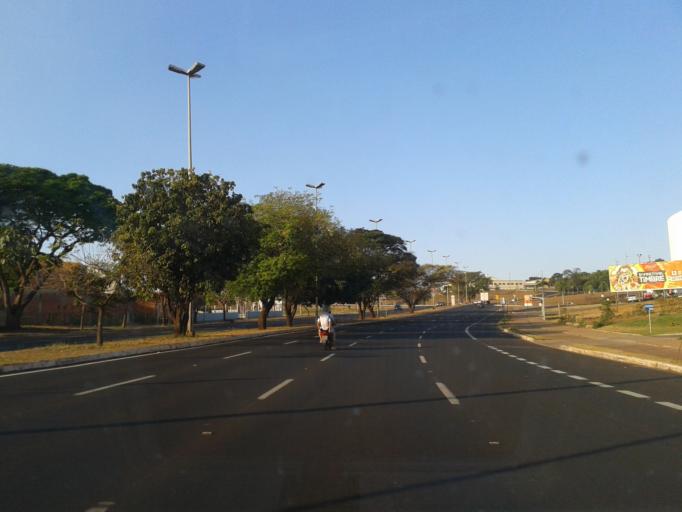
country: BR
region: Minas Gerais
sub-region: Uberlandia
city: Uberlandia
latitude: -18.8958
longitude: -48.2543
